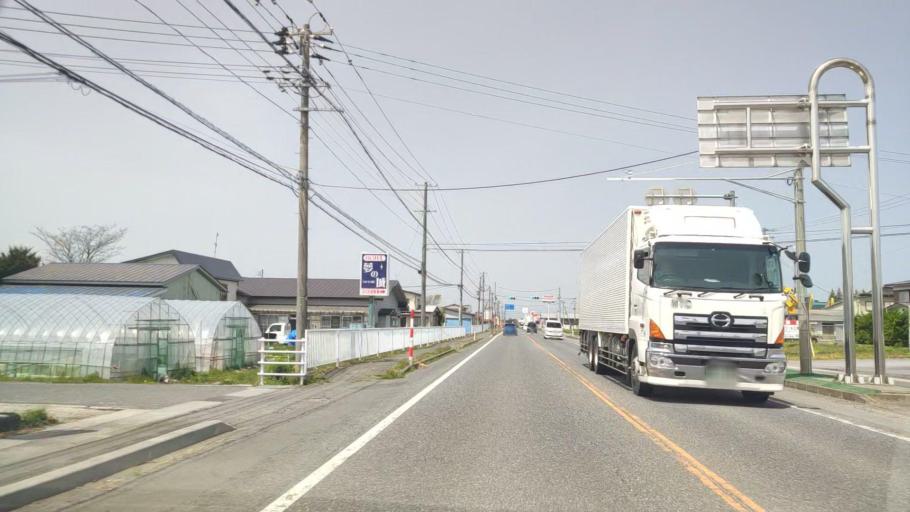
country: JP
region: Aomori
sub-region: Misawa Shi
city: Inuotose
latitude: 40.6471
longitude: 141.1975
